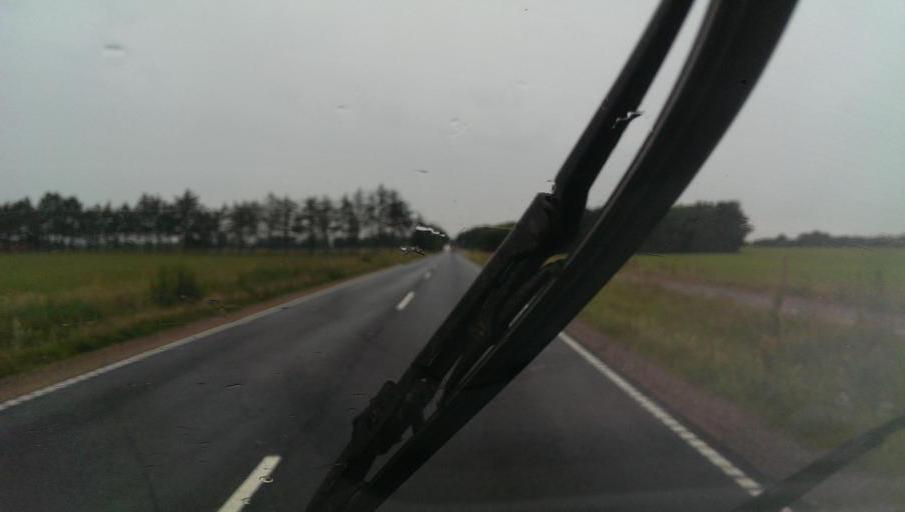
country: DK
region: South Denmark
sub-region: Varde Kommune
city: Oksbol
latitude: 55.6794
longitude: 8.3701
